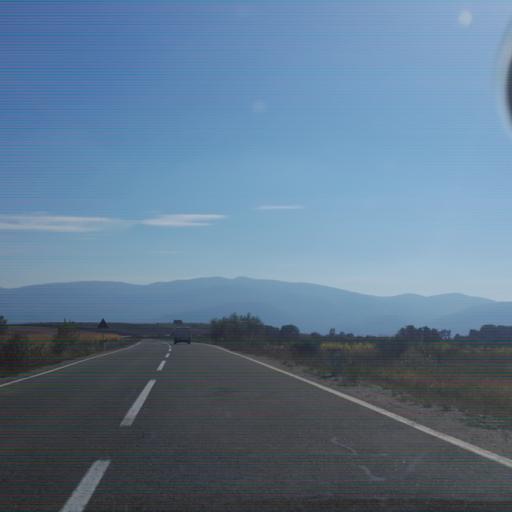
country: RS
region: Central Serbia
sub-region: Nisavski Okrug
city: Svrljig
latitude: 43.4496
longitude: 22.1711
